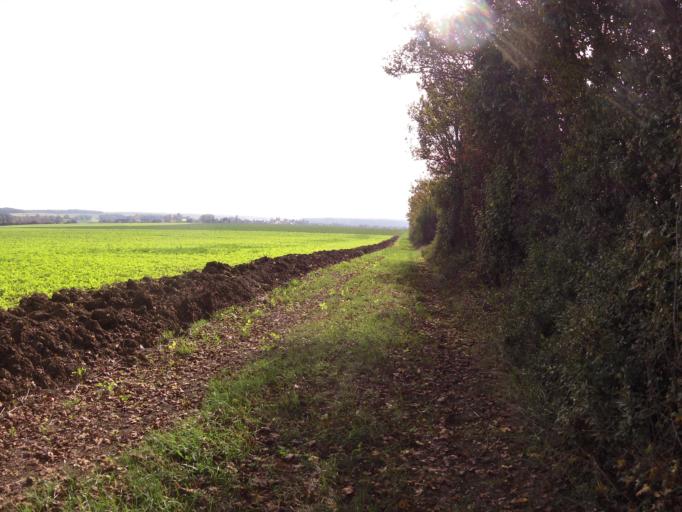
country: DE
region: Bavaria
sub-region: Regierungsbezirk Unterfranken
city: Frickenhausen
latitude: 49.7156
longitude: 10.0733
